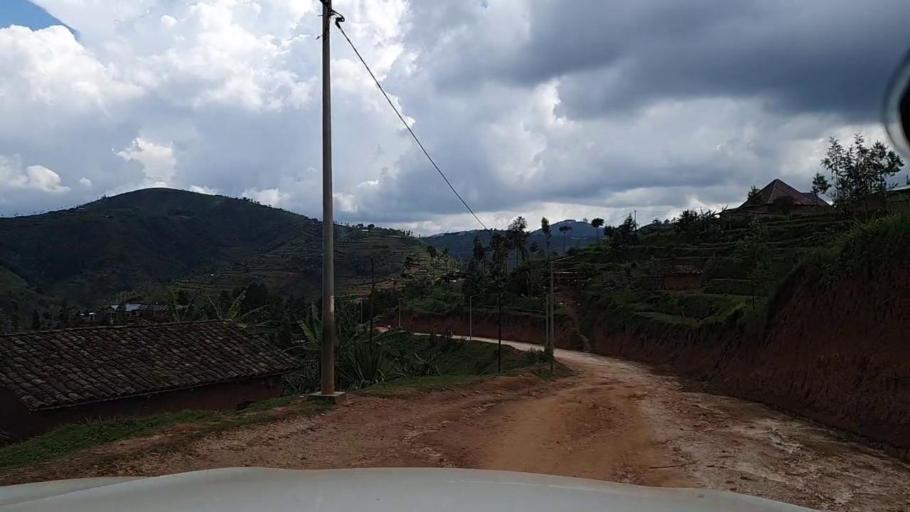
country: RW
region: Southern Province
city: Nzega
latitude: -2.6920
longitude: 29.4434
